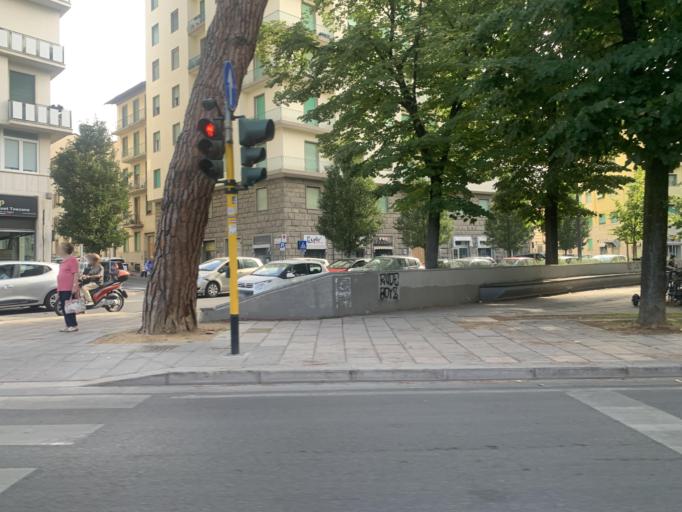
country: IT
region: Tuscany
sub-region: Province of Florence
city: Florence
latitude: 43.7915
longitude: 11.2474
